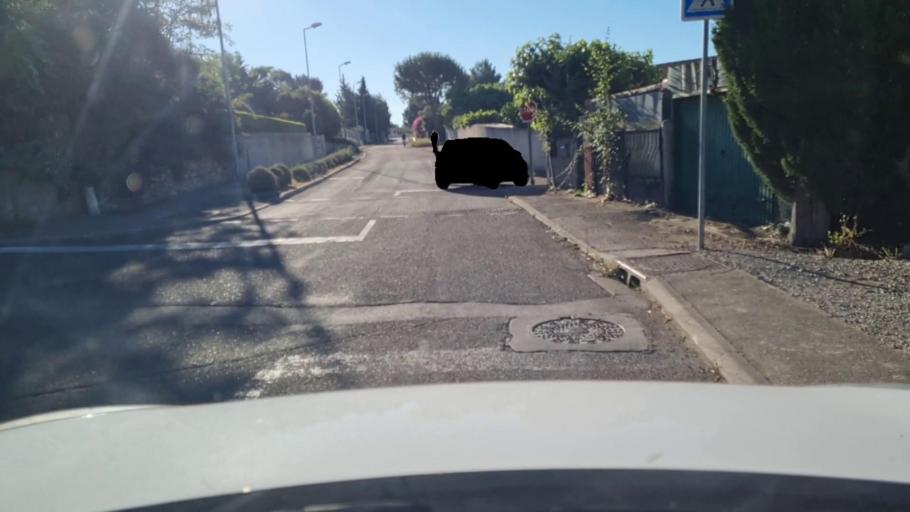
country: FR
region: Languedoc-Roussillon
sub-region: Departement du Gard
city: Caveirac
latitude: 43.8285
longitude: 4.2556
